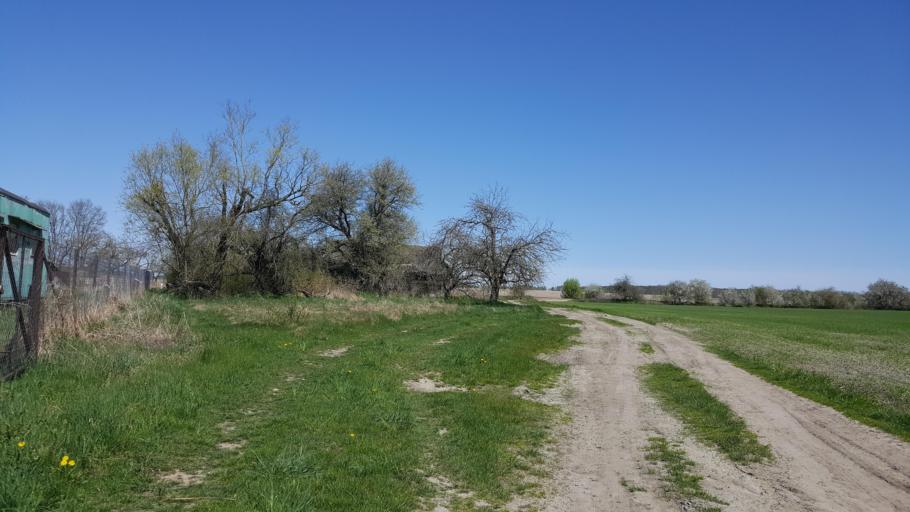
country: BY
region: Brest
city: Kamyanyets
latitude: 52.3271
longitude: 23.7612
